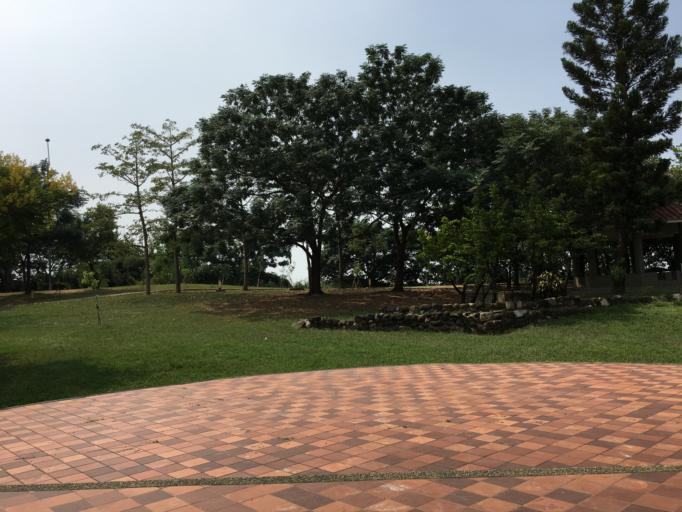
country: TW
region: Taiwan
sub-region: Chiayi
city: Jiayi Shi
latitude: 23.5447
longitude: 120.4313
